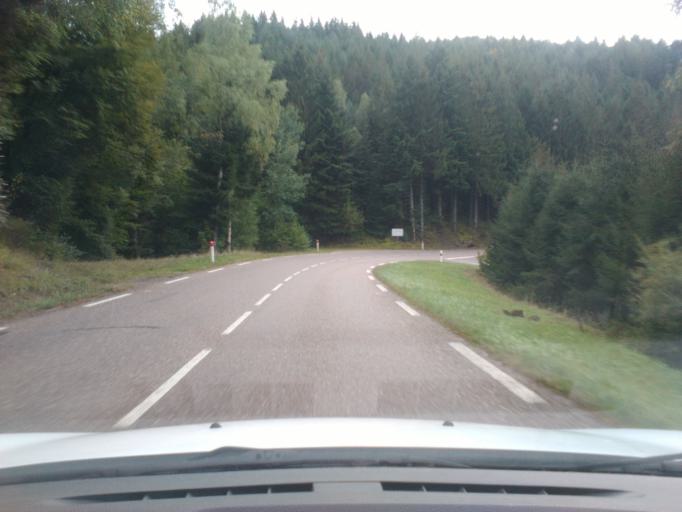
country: FR
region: Lorraine
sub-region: Departement des Vosges
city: Taintrux
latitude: 48.2721
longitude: 6.8348
